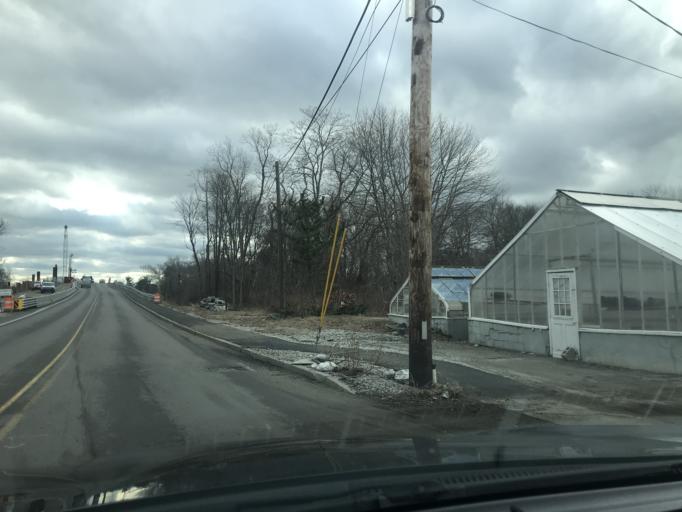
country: US
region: Massachusetts
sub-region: Plymouth County
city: Rockland
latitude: 42.1604
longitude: -70.9553
